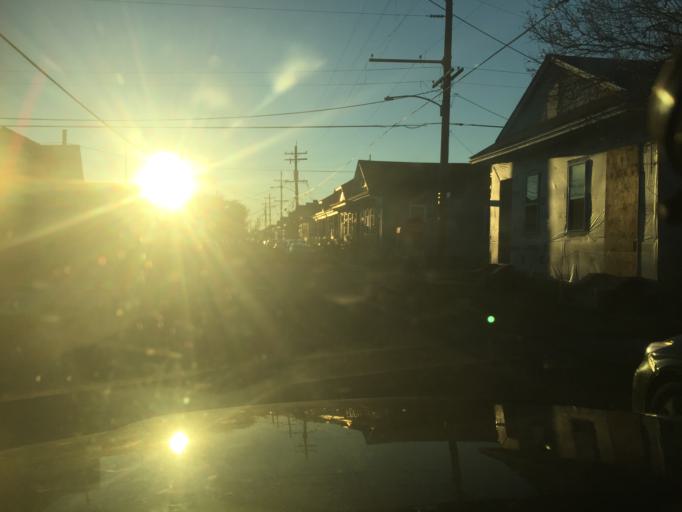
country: US
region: Louisiana
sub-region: Orleans Parish
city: New Orleans
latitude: 29.9746
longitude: -90.0871
